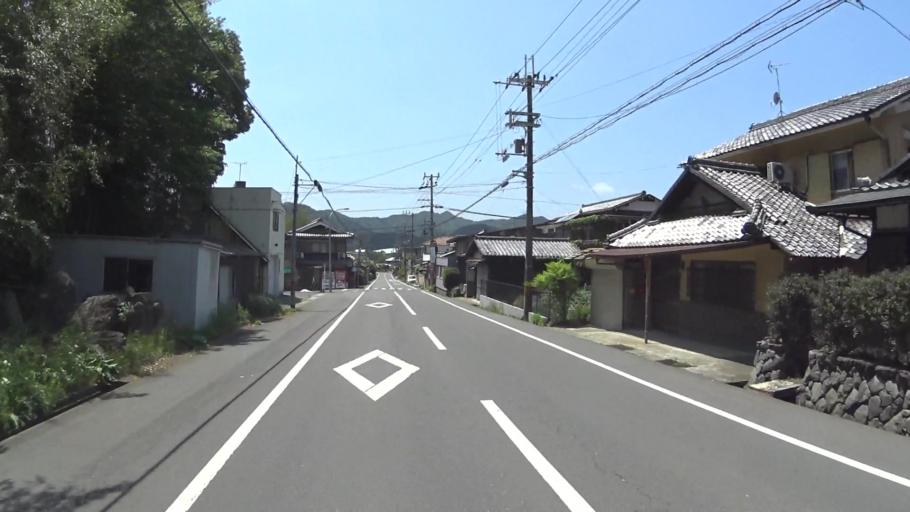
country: JP
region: Kyoto
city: Kameoka
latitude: 35.0765
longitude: 135.5431
